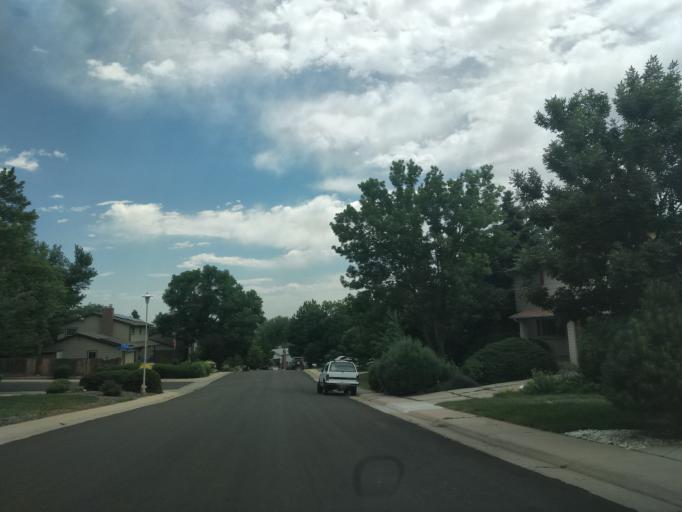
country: US
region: Colorado
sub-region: Jefferson County
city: Lakewood
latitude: 39.6736
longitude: -105.1038
